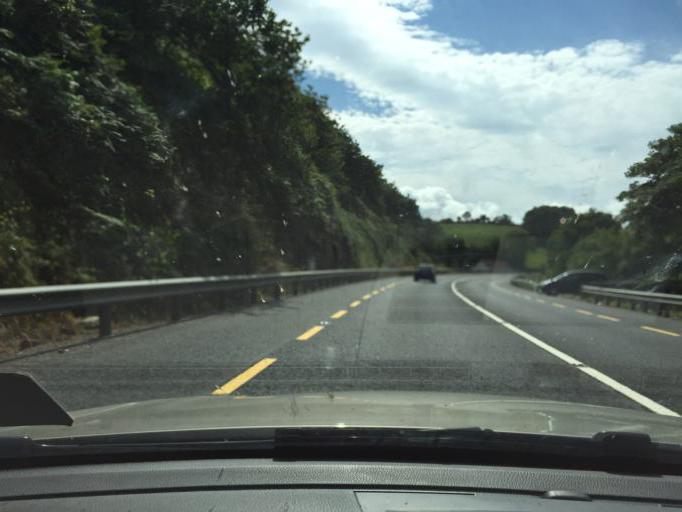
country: IE
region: Munster
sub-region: Waterford
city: Portlaw
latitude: 52.2371
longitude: -7.2855
